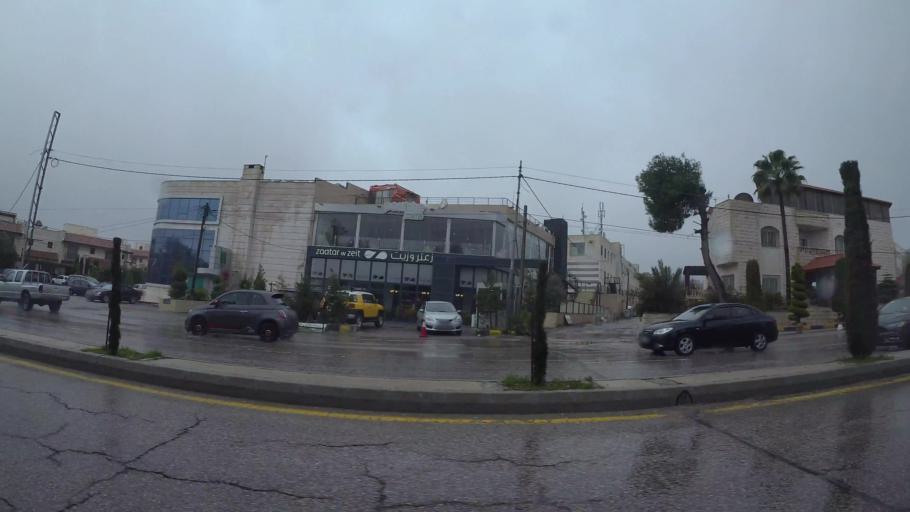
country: JO
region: Amman
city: Wadi as Sir
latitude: 31.9957
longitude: 35.8137
